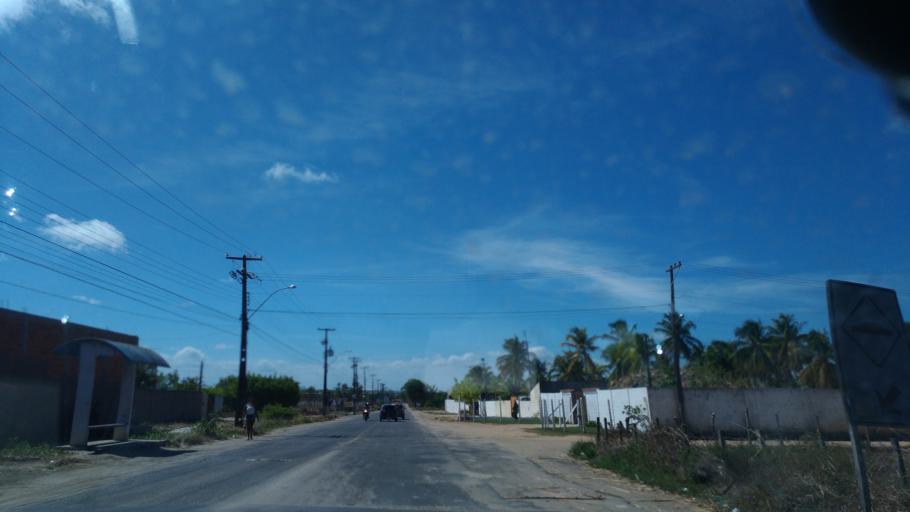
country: BR
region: Alagoas
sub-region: Marechal Deodoro
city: Marechal Deodoro
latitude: -9.7481
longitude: -35.8776
